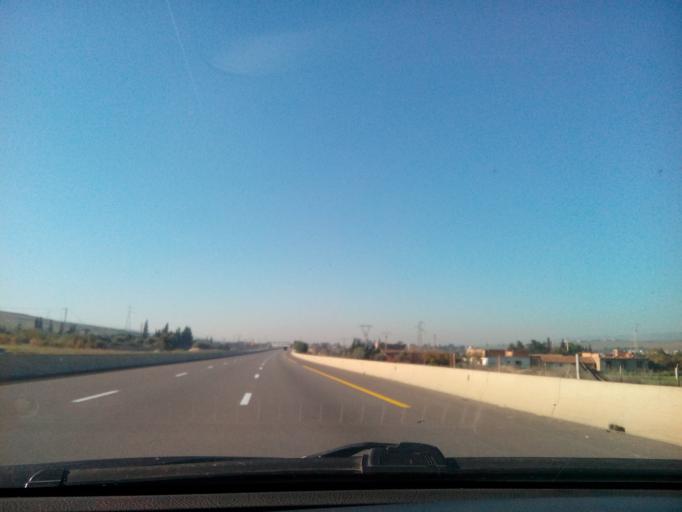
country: DZ
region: Chlef
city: Boukadir
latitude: 36.0350
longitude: 1.0802
